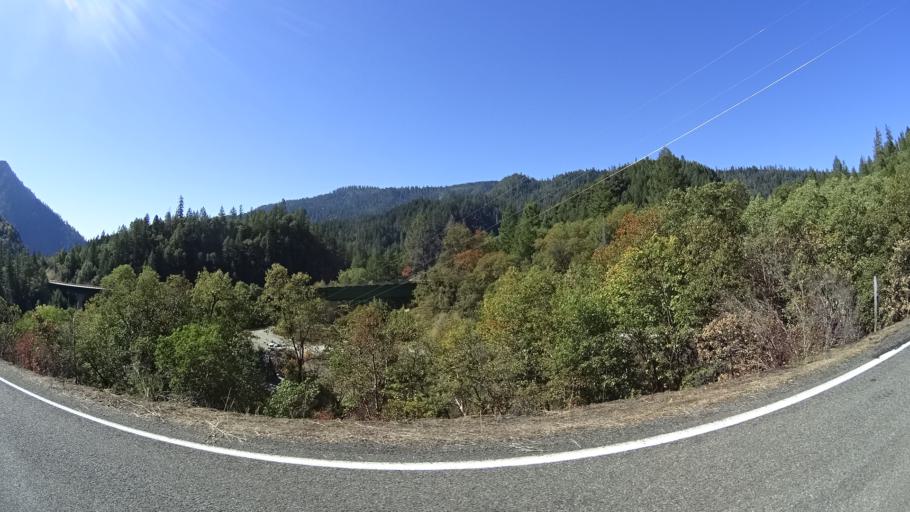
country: US
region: California
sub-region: Siskiyou County
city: Happy Camp
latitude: 41.3803
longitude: -123.4871
